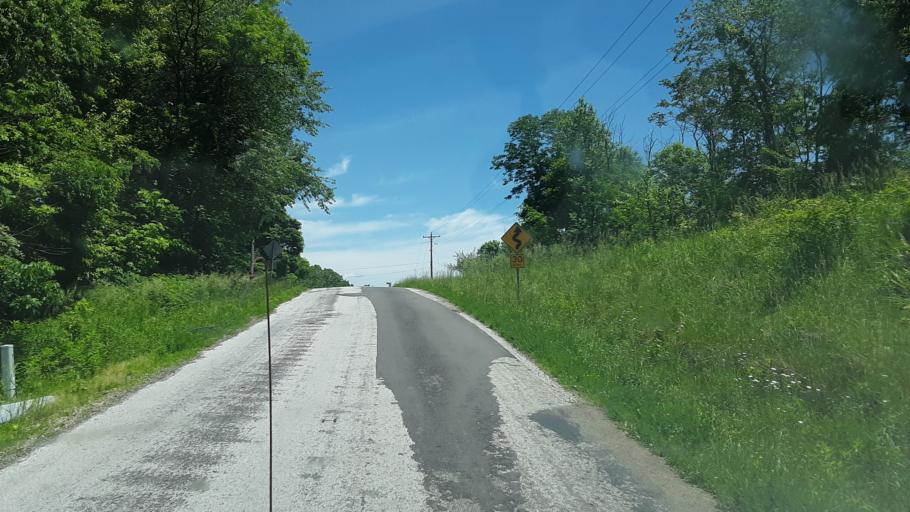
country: US
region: Ohio
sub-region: Coshocton County
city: Coshocton
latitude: 40.2687
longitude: -81.9263
